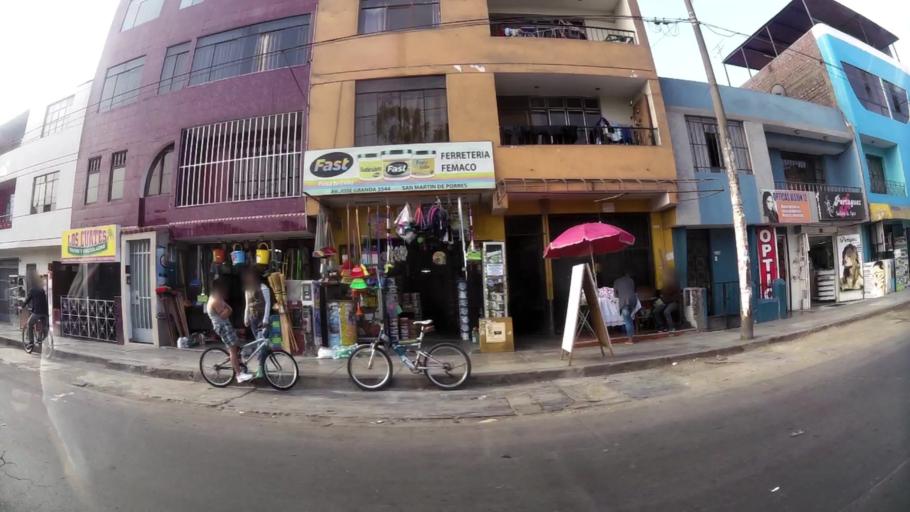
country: PE
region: Callao
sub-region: Callao
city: Callao
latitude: -12.0224
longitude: -77.0838
